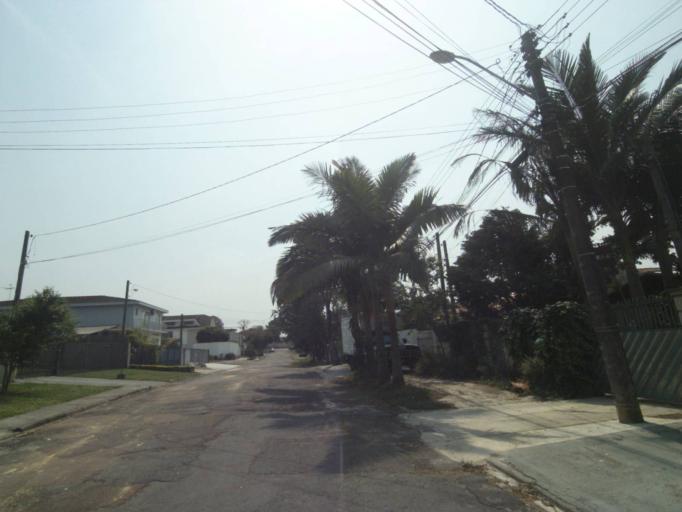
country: BR
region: Parana
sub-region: Sao Jose Dos Pinhais
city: Sao Jose dos Pinhais
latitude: -25.4890
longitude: -49.2132
